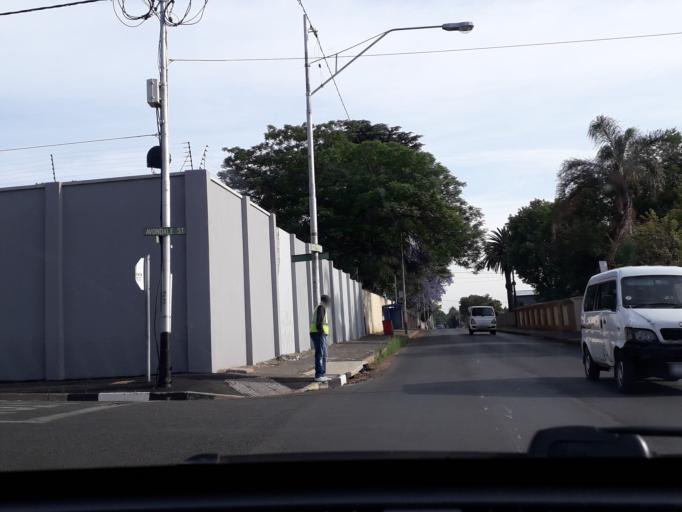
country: ZA
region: Gauteng
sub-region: City of Johannesburg Metropolitan Municipality
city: Johannesburg
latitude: -26.1553
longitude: 28.0960
